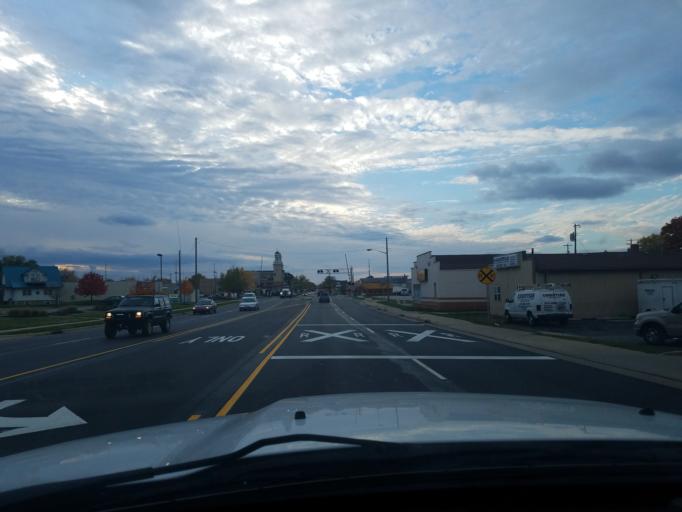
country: US
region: Indiana
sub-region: Shelby County
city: Shelbyville
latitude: 39.5230
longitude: -85.7693
